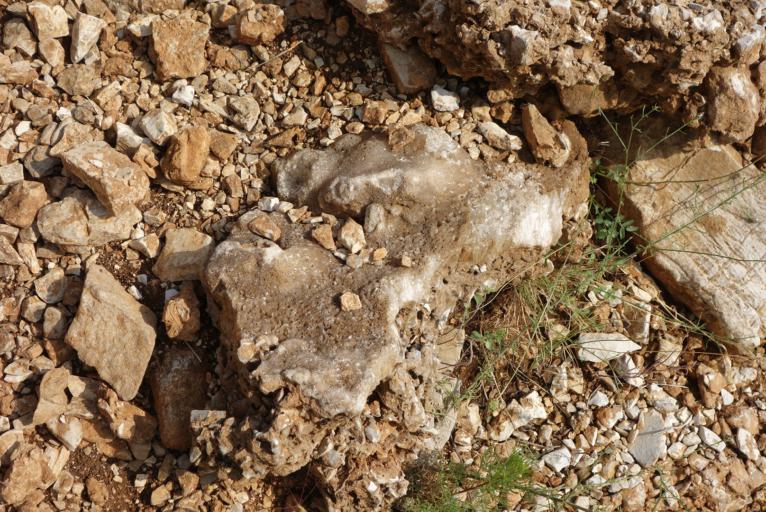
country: AL
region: Gjirokaster
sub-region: Rrethi i Permetit
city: Permet
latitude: 40.1835
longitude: 20.3315
